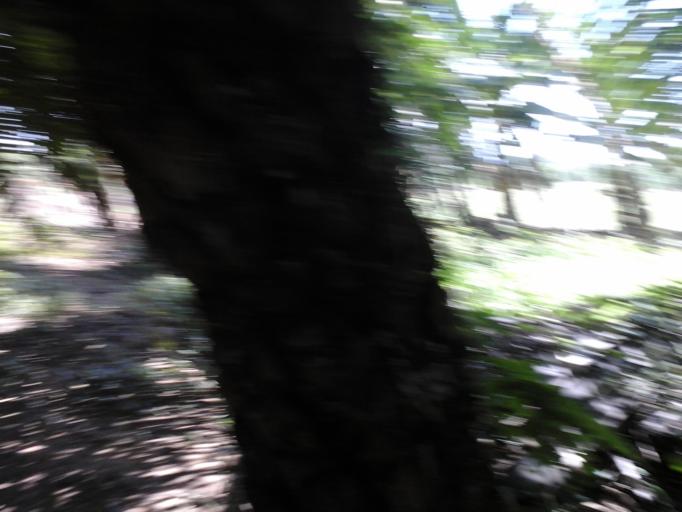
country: CO
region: Bolivar
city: San Pablo
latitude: 10.1611
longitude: -75.2736
